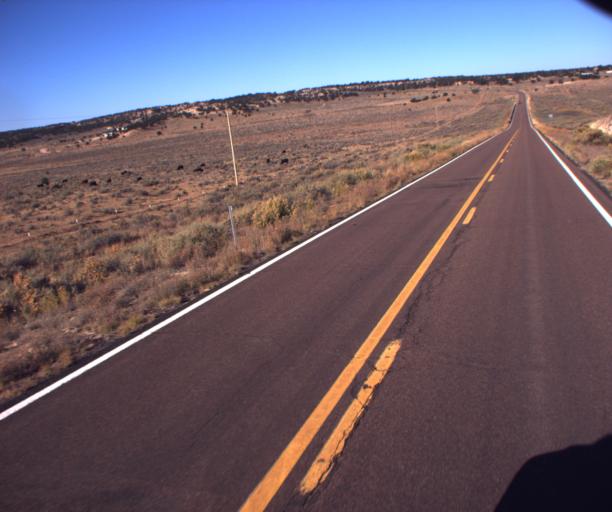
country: US
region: Arizona
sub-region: Navajo County
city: First Mesa
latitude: 35.7641
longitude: -109.9783
